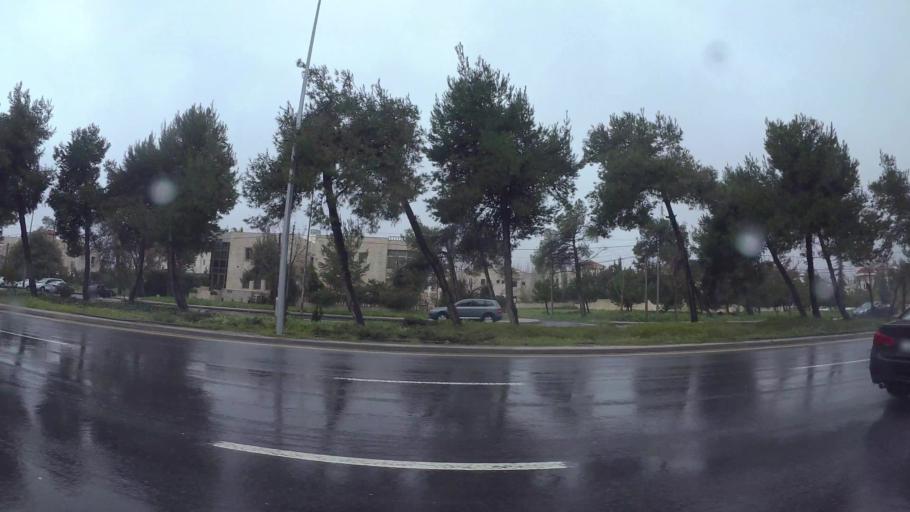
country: JO
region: Amman
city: Wadi as Sir
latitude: 31.9930
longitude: 35.8252
